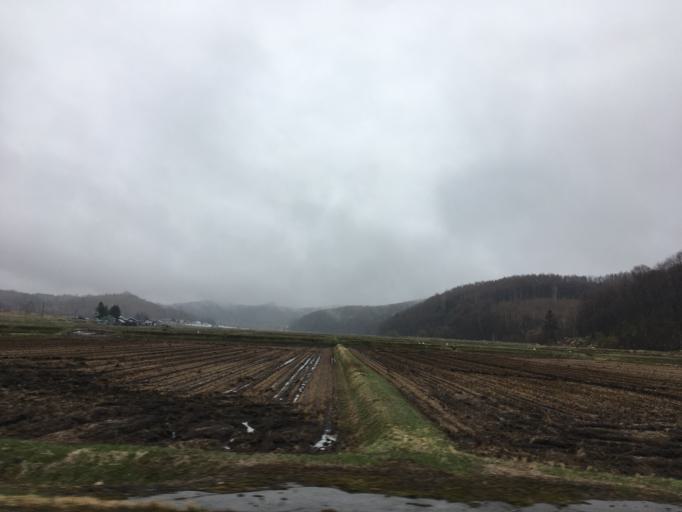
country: JP
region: Hokkaido
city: Nayoro
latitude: 44.0803
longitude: 142.4187
